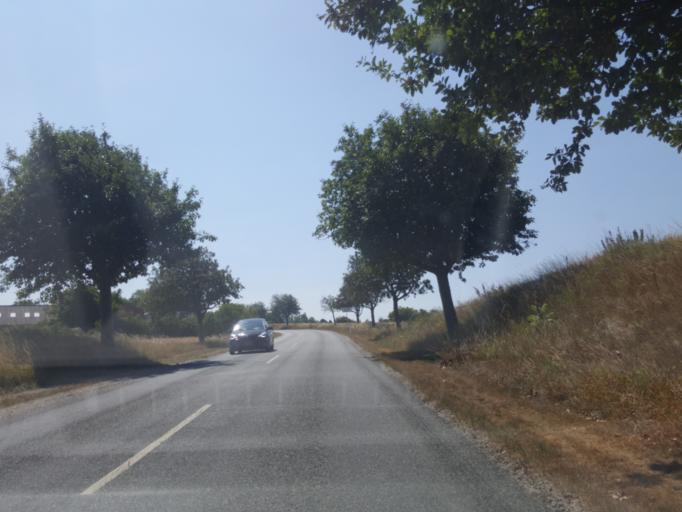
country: DK
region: Capital Region
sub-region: Fredensborg Kommune
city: Niva
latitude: 55.9320
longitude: 12.4703
